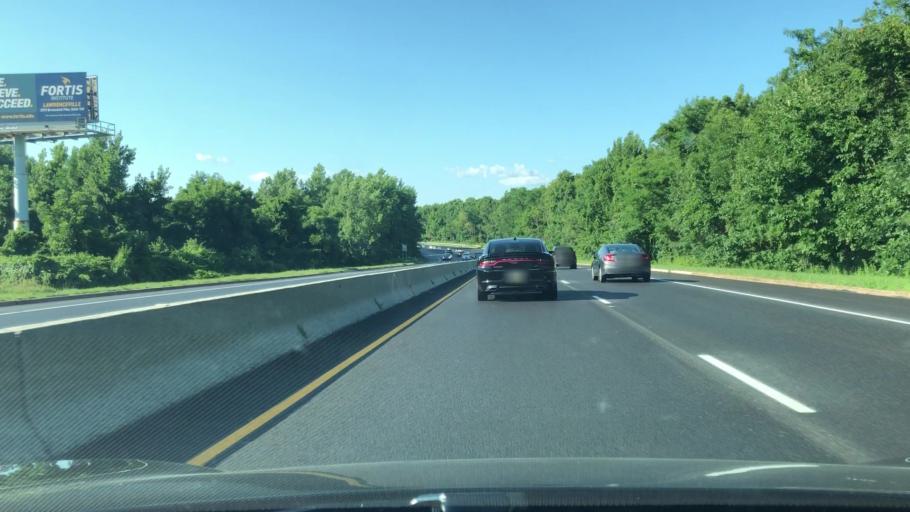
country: US
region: New Jersey
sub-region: Mercer County
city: Lawrenceville
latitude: 40.2620
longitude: -74.7161
